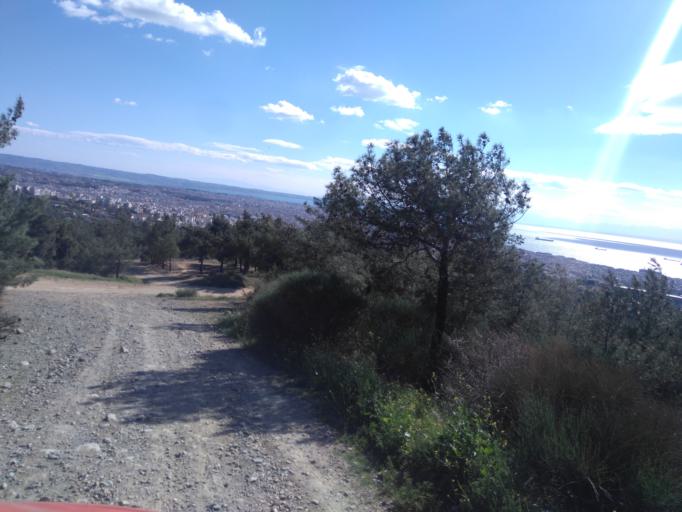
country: GR
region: Central Macedonia
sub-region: Nomos Thessalonikis
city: Triandria
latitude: 40.6313
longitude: 22.9786
